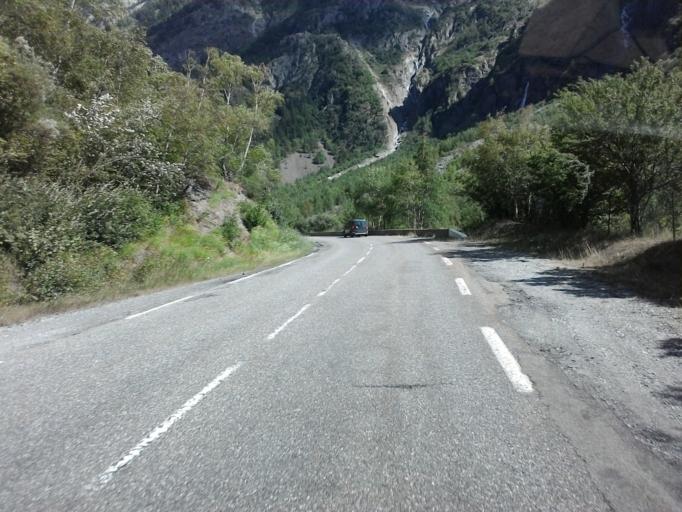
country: FR
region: Rhone-Alpes
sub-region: Departement de l'Isere
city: Mont-de-Lans
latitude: 45.0367
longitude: 6.2156
